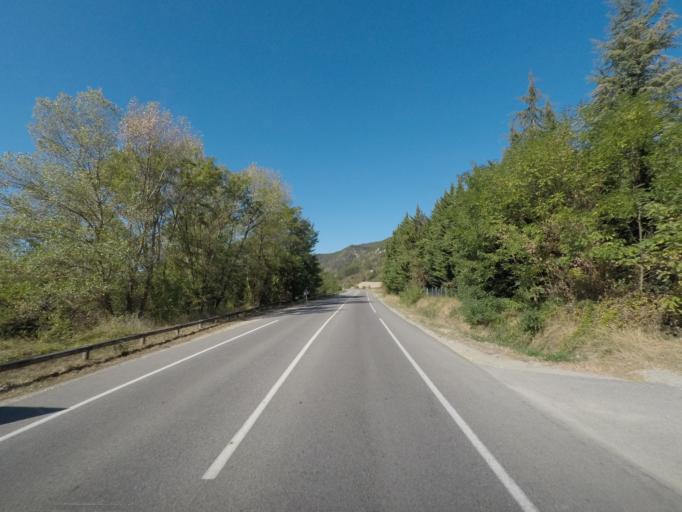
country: FR
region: Rhone-Alpes
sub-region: Departement de la Drome
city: Aouste-sur-Sye
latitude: 44.6946
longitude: 5.1687
